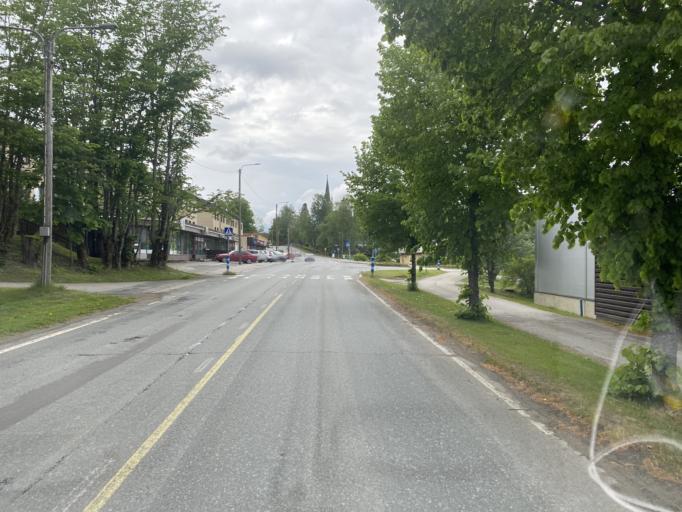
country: FI
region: Pirkanmaa
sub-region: Etelae-Pirkanmaa
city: Urjala
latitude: 61.0801
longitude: 23.5500
